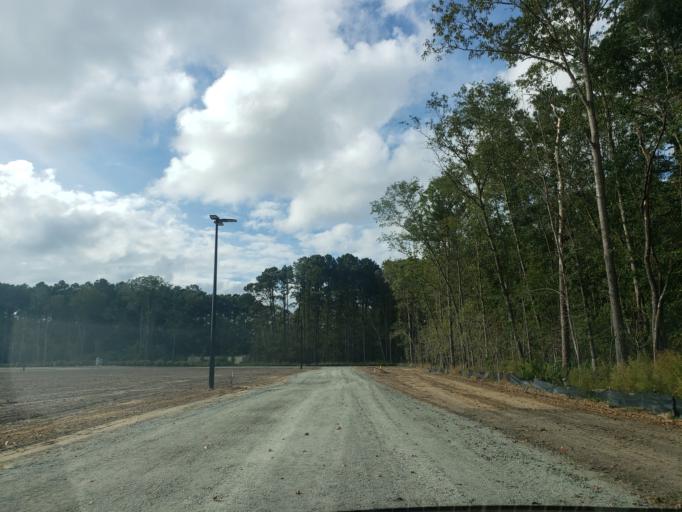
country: US
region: Georgia
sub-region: Bryan County
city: Richmond Hill
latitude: 32.0074
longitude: -81.2942
